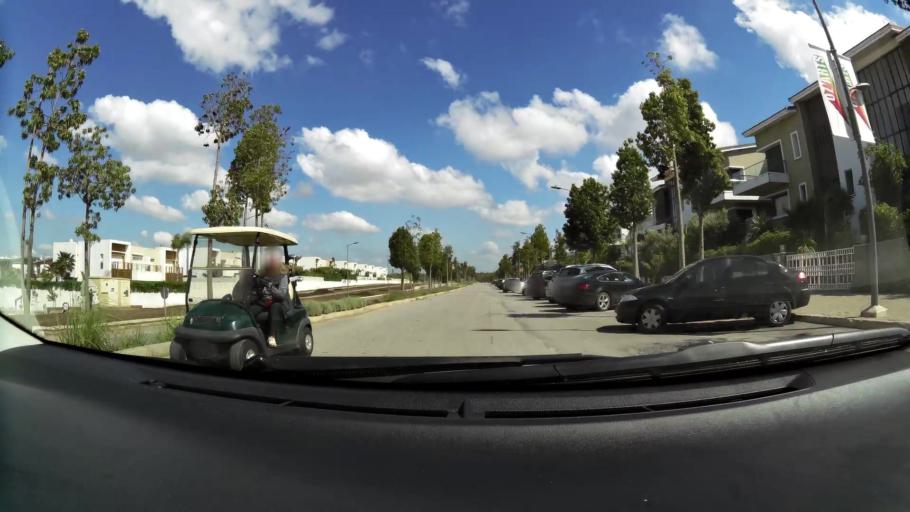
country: MA
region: Grand Casablanca
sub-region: Nouaceur
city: Bouskoura
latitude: 33.4830
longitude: -7.5917
